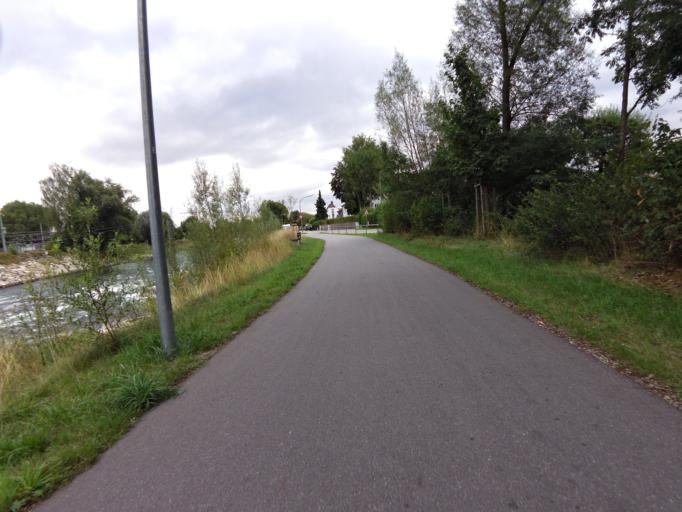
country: DE
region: Bavaria
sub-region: Lower Bavaria
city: Landshut
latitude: 48.5461
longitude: 12.1641
